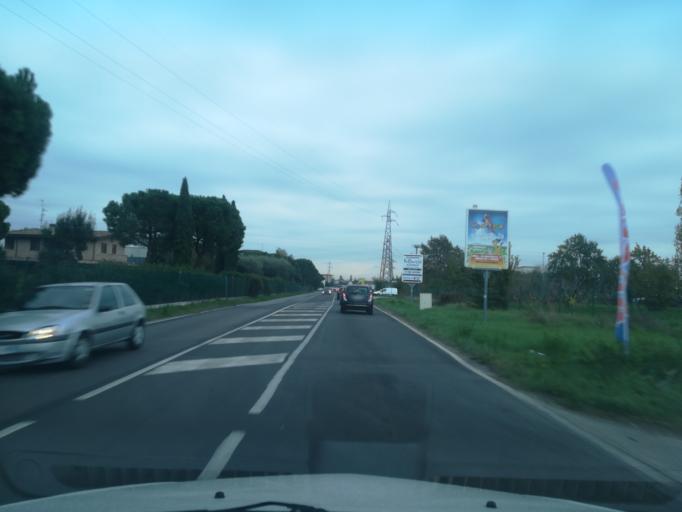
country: IT
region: Emilia-Romagna
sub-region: Provincia di Bologna
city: Imola
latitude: 44.3700
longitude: 11.7085
